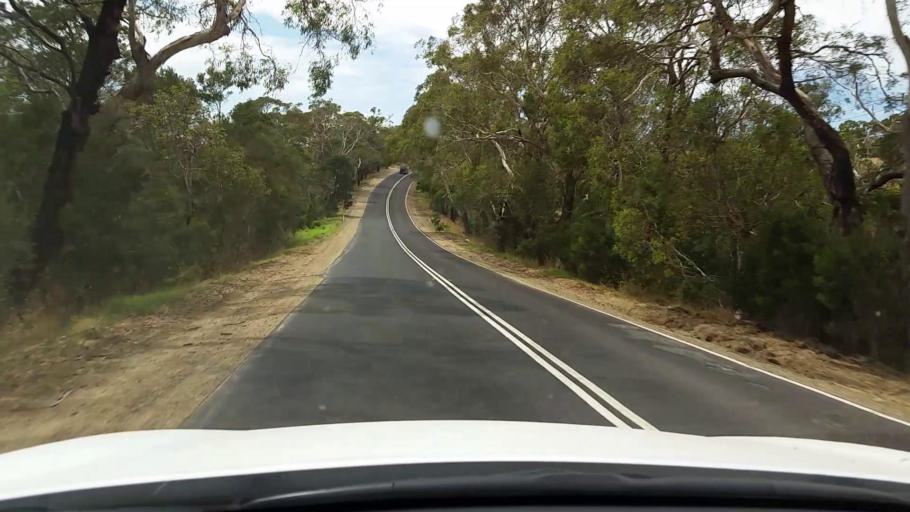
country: AU
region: Victoria
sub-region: Mornington Peninsula
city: Mount Martha
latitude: -38.2978
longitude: 145.0447
